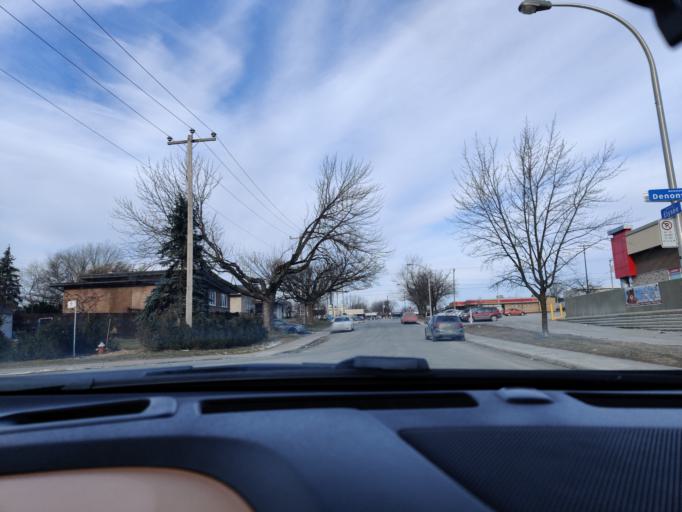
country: CA
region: Quebec
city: Dollard-Des Ormeaux
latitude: 45.5276
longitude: -73.7574
